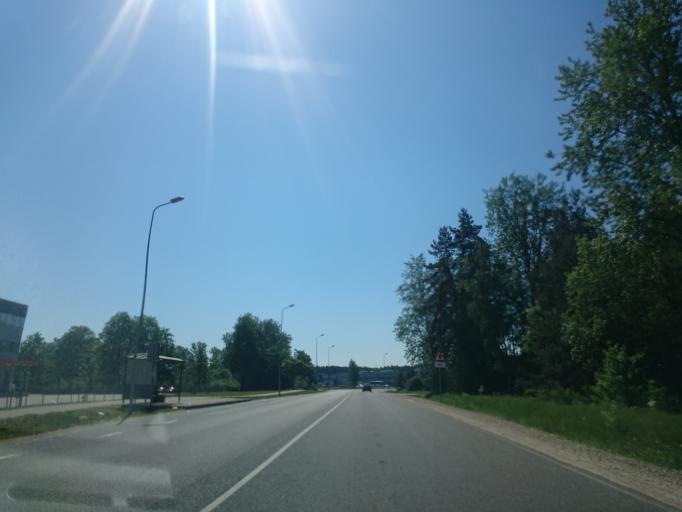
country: LV
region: Kekava
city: Balozi
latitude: 56.8920
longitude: 24.1481
